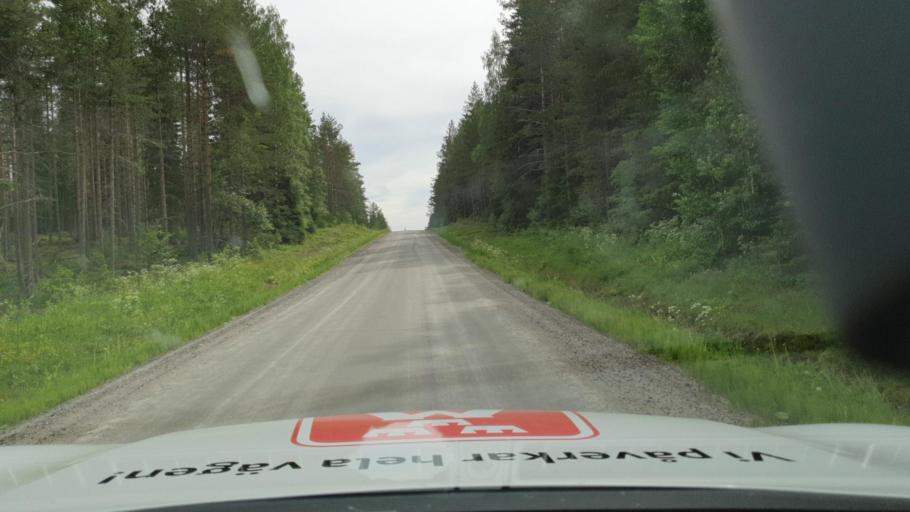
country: SE
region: Vaesterbotten
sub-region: Skelleftea Kommun
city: Burea
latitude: 64.4247
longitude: 21.0122
